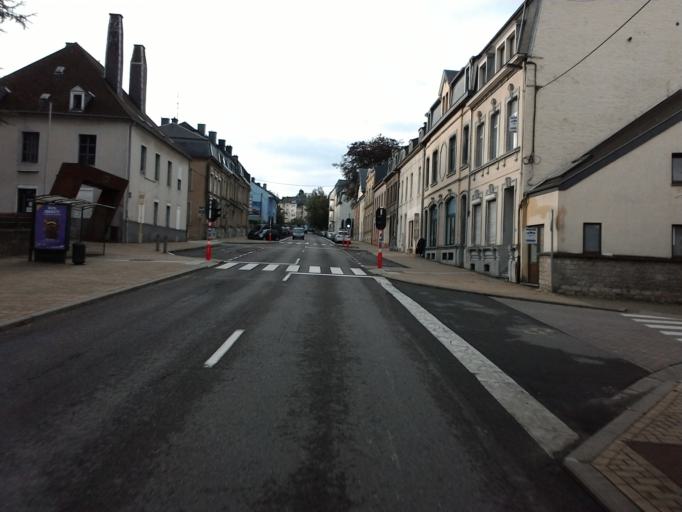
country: BE
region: Wallonia
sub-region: Province du Luxembourg
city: Arlon
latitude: 49.6878
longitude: 5.8102
